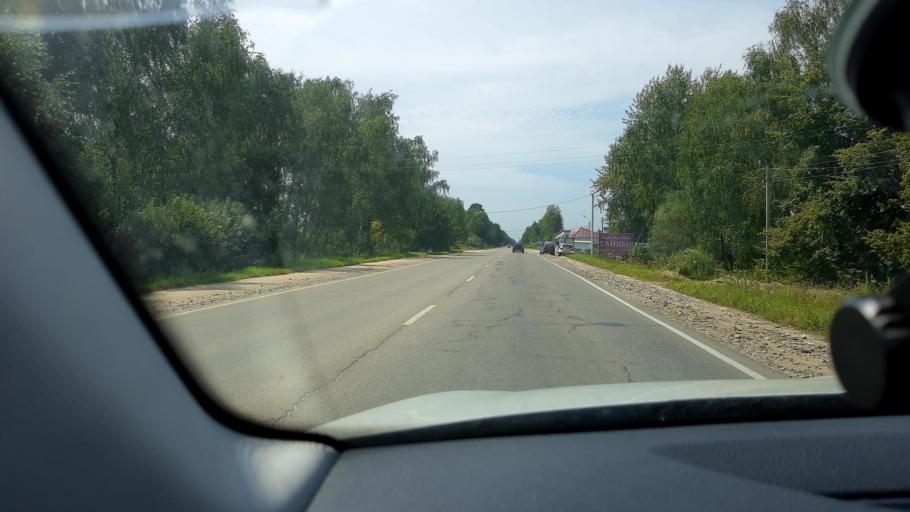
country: RU
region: Tula
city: Zaokskiy
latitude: 54.7421
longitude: 37.3832
